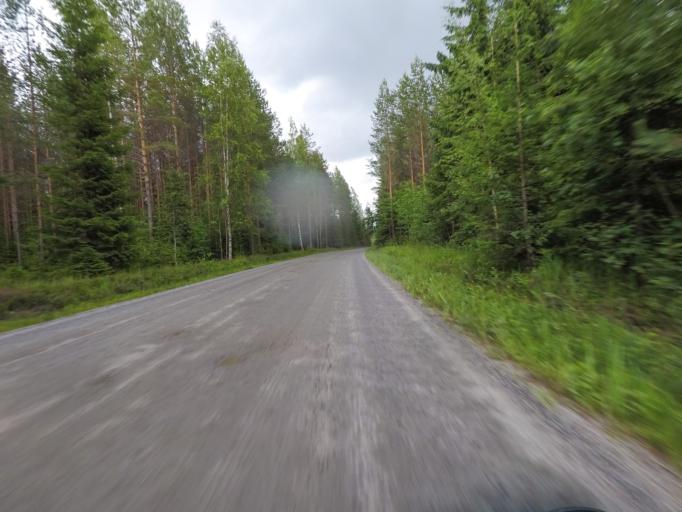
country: FI
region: Central Finland
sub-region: Jyvaeskylae
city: Hankasalmi
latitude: 62.3927
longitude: 26.6002
